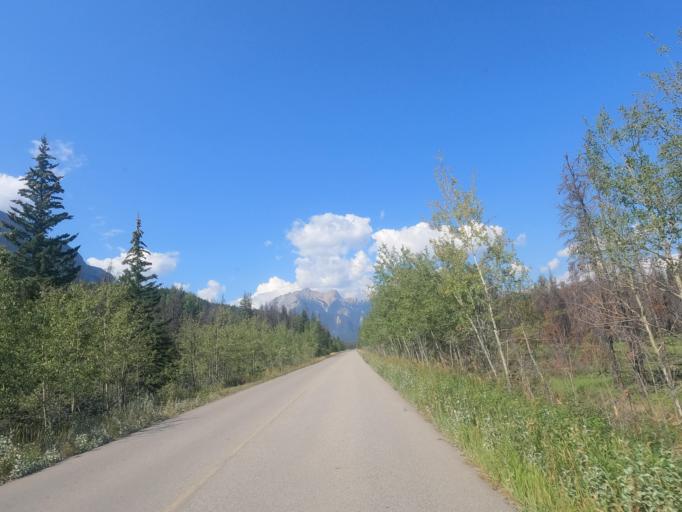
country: CA
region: Alberta
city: Jasper Park Lodge
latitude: 52.9814
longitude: -118.0726
